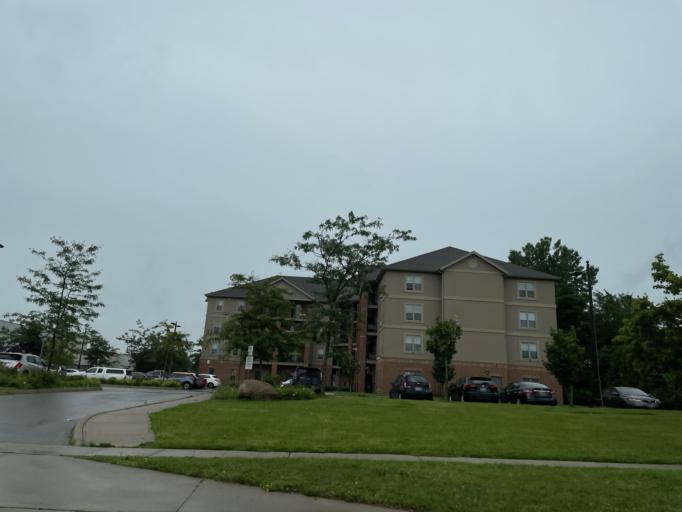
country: CA
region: Ontario
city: Cambridge
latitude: 43.3935
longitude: -80.3052
